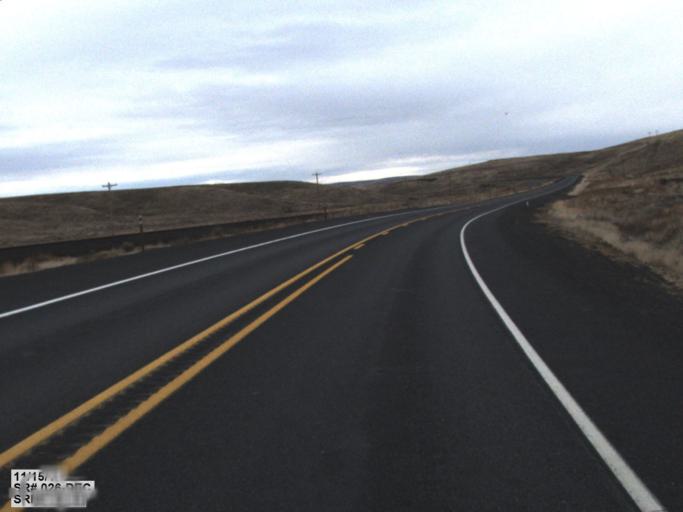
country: US
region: Washington
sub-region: Columbia County
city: Dayton
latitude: 46.7625
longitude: -117.9932
